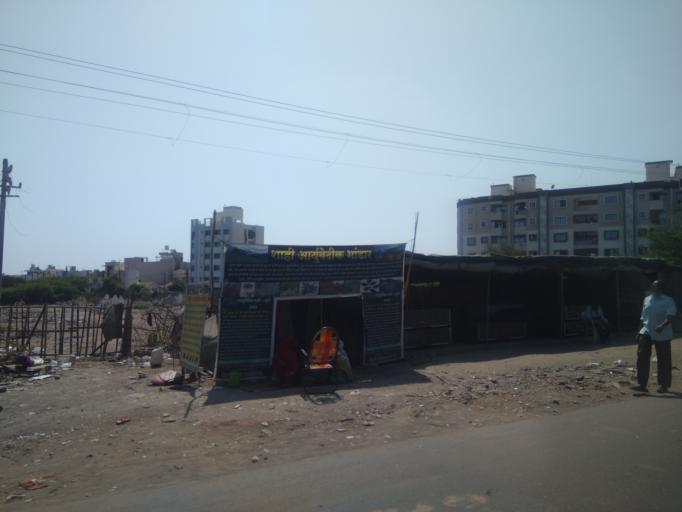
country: IN
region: Gujarat
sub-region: Jamnagar
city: Jamnagar
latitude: 22.4488
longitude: 70.0674
